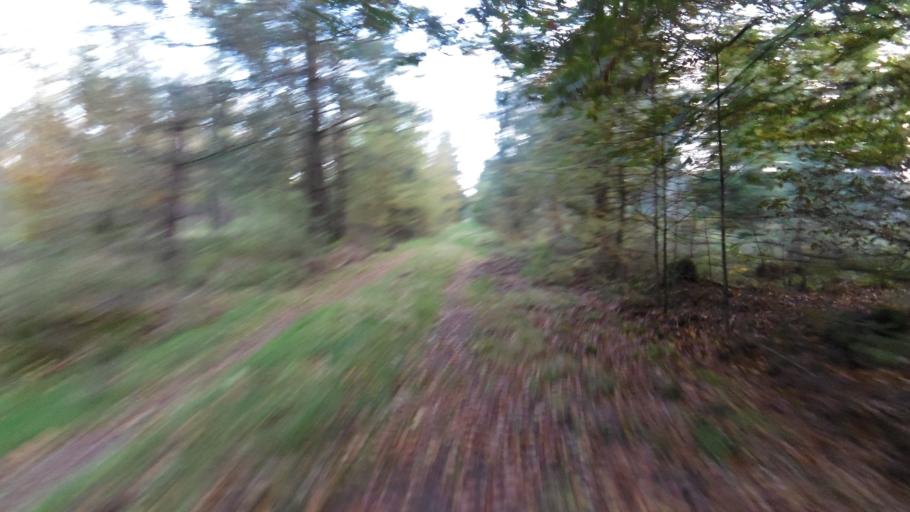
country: NL
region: Gelderland
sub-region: Gemeente Epe
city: Emst
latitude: 52.3518
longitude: 5.8994
